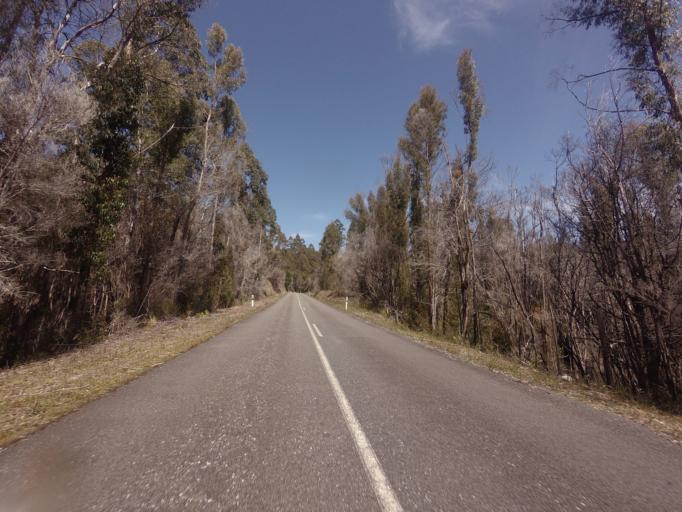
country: AU
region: Tasmania
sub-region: Huon Valley
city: Geeveston
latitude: -42.8345
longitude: 146.2672
